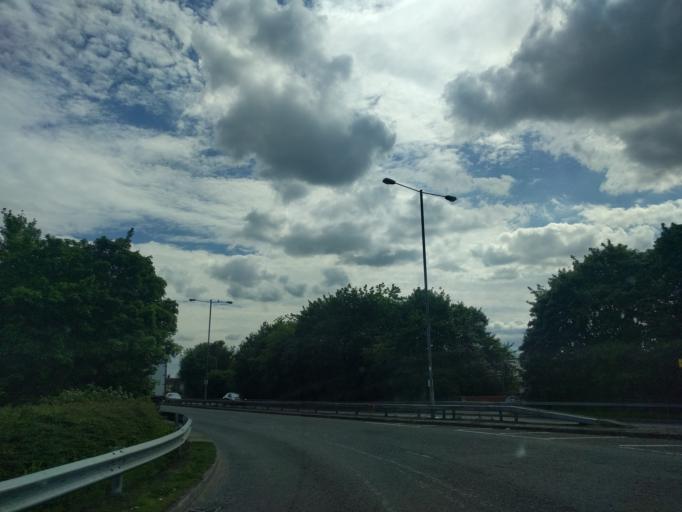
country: GB
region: England
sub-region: Borough of Swindon
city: Swindon
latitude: 51.5758
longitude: -1.7713
